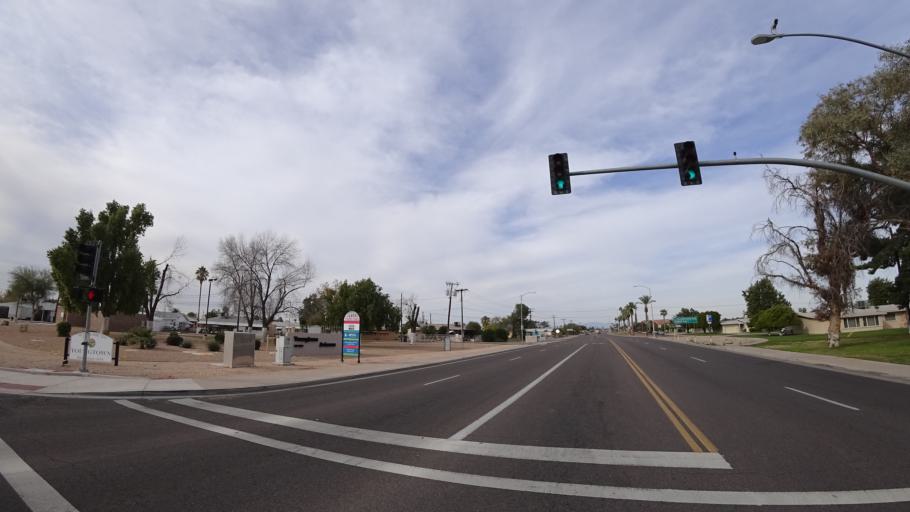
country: US
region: Arizona
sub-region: Maricopa County
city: Youngtown
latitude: 33.5801
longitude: -112.2987
